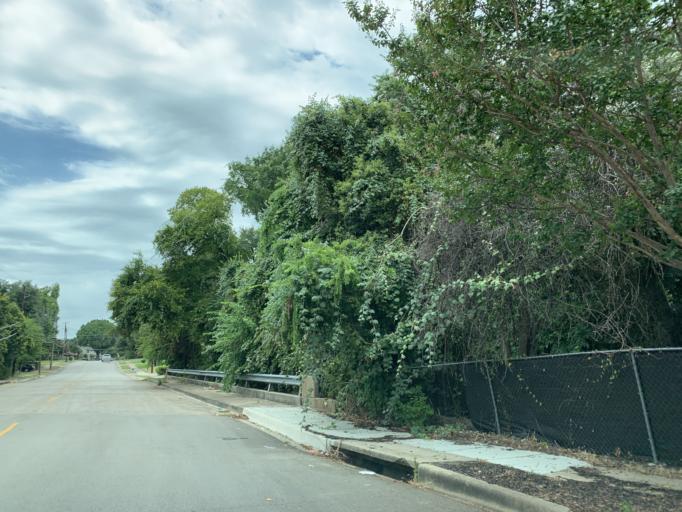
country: US
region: Texas
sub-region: Dallas County
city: DeSoto
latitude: 32.6544
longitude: -96.8278
